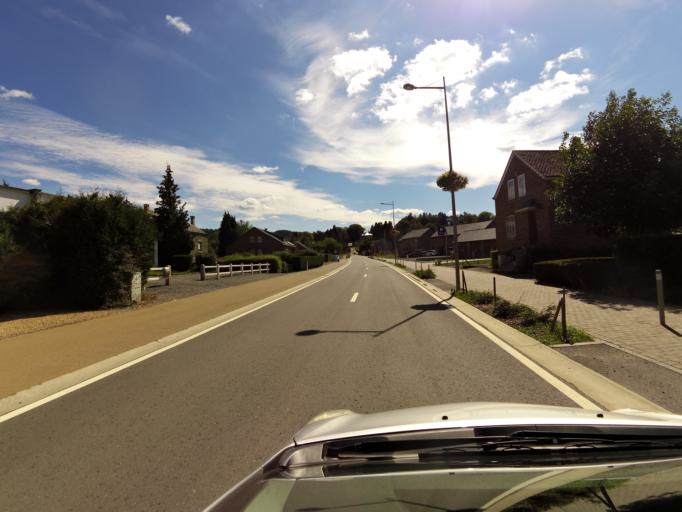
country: BE
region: Wallonia
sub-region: Province du Luxembourg
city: Rendeux
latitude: 50.2322
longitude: 5.5135
